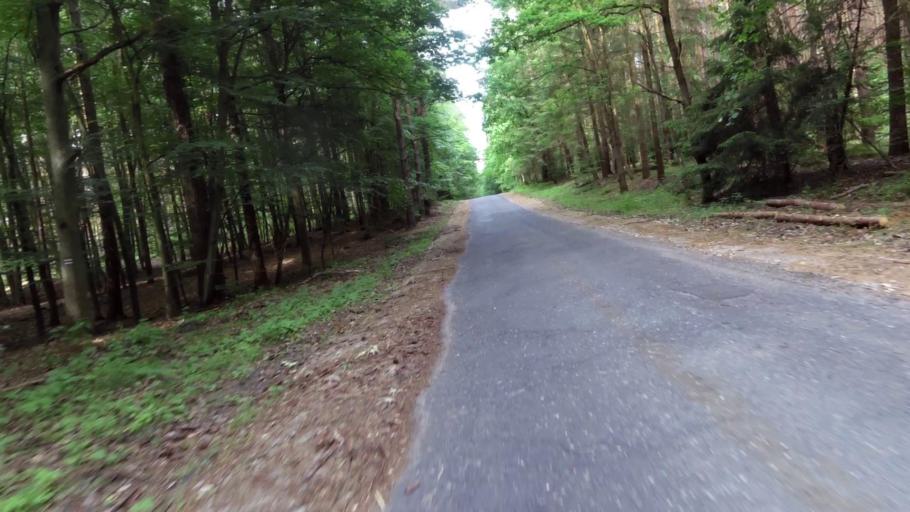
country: PL
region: West Pomeranian Voivodeship
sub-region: Powiat mysliborski
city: Debno
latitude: 52.8074
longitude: 14.6631
